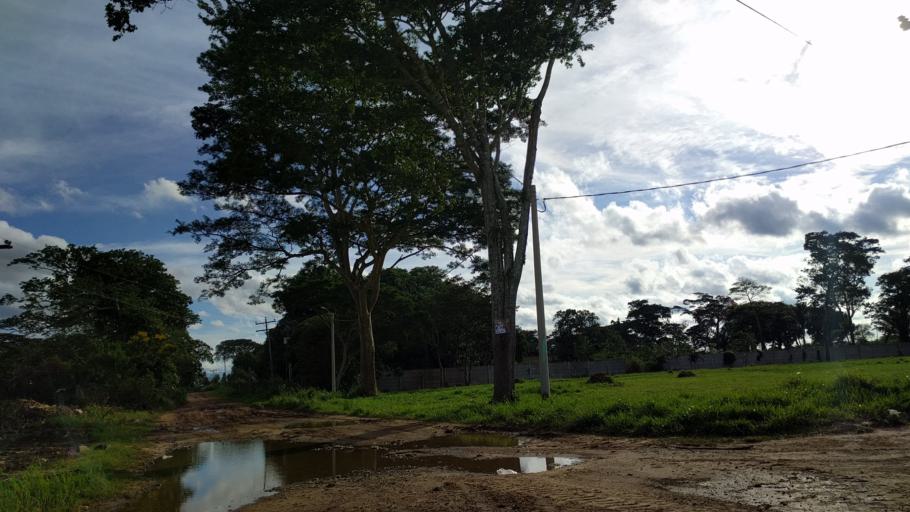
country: BO
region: Santa Cruz
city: Santa Cruz de la Sierra
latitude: -17.8521
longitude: -63.2604
